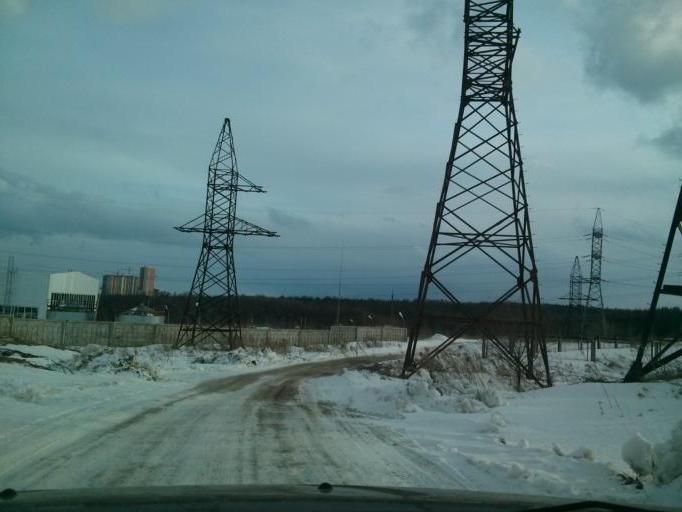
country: RU
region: Nizjnij Novgorod
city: Afonino
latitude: 56.2647
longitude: 44.0311
